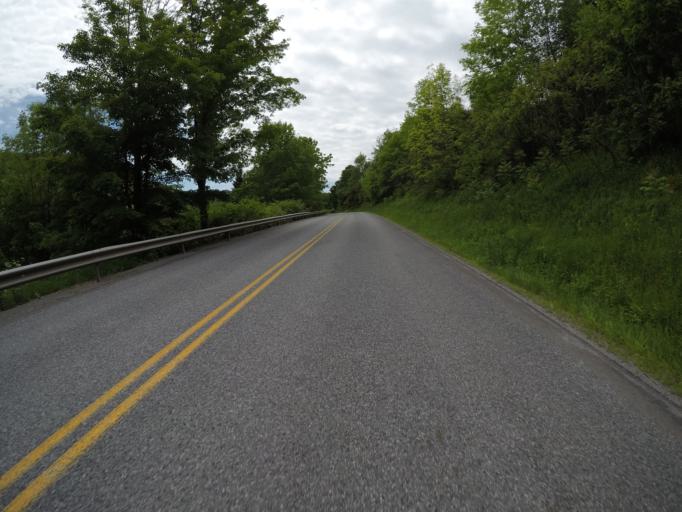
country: US
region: New York
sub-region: Delaware County
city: Stamford
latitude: 42.1947
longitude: -74.5805
